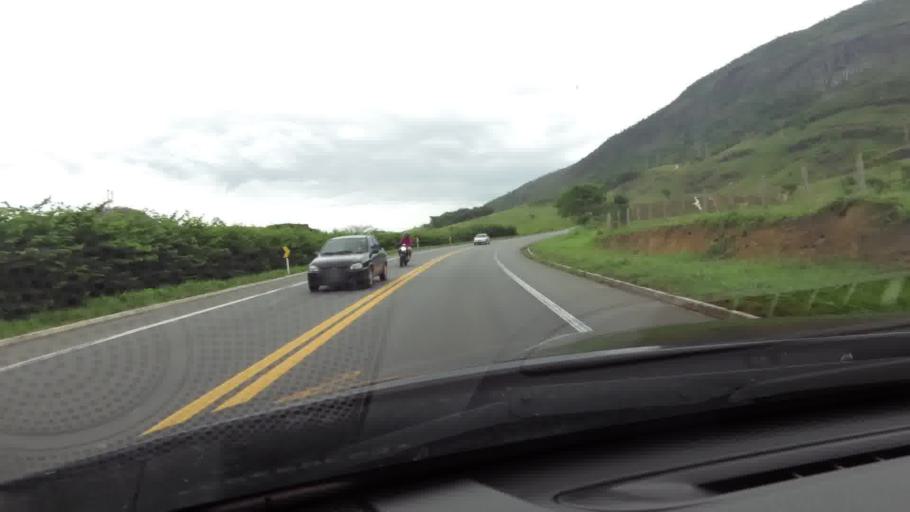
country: BR
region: Espirito Santo
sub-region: Guarapari
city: Guarapari
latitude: -20.6053
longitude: -40.5046
